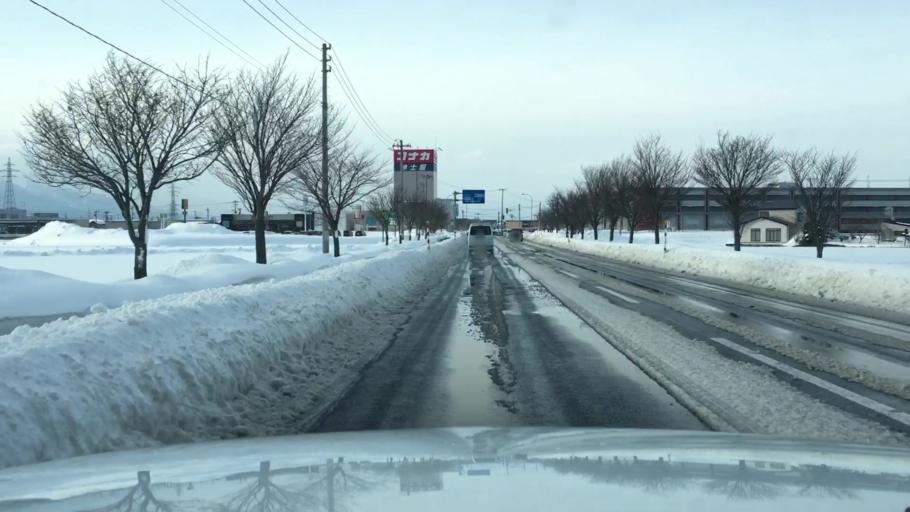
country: JP
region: Aomori
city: Hirosaki
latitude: 40.5973
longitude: 140.5156
